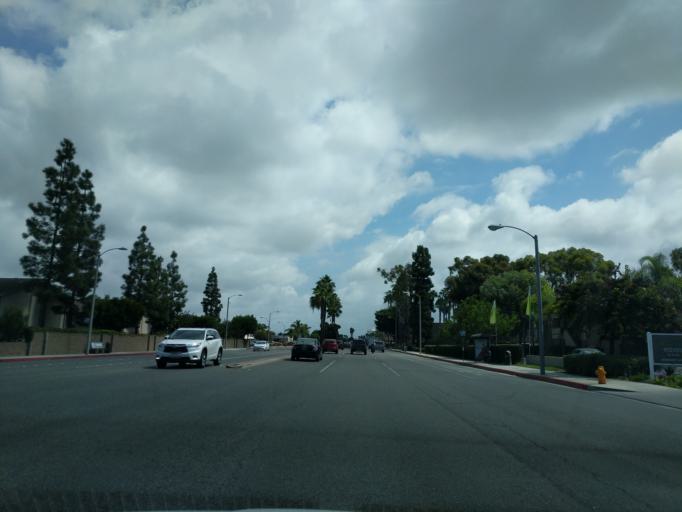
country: US
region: California
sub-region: Orange County
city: Midway City
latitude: 33.7155
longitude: -118.0123
